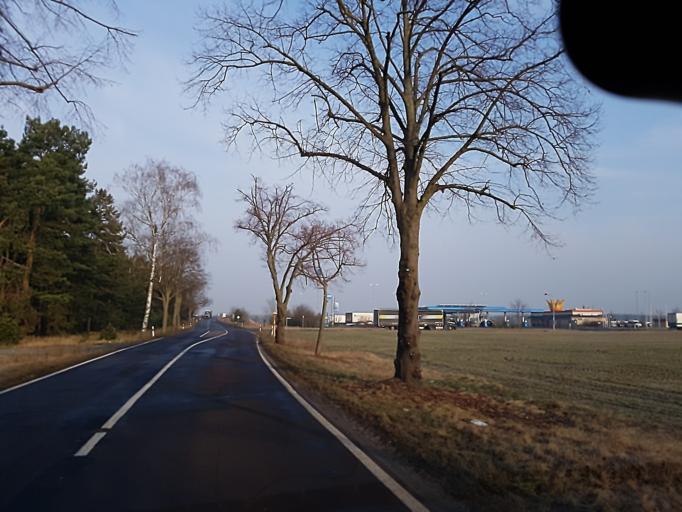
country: DE
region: Brandenburg
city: Wollin
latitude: 52.2875
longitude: 12.4644
